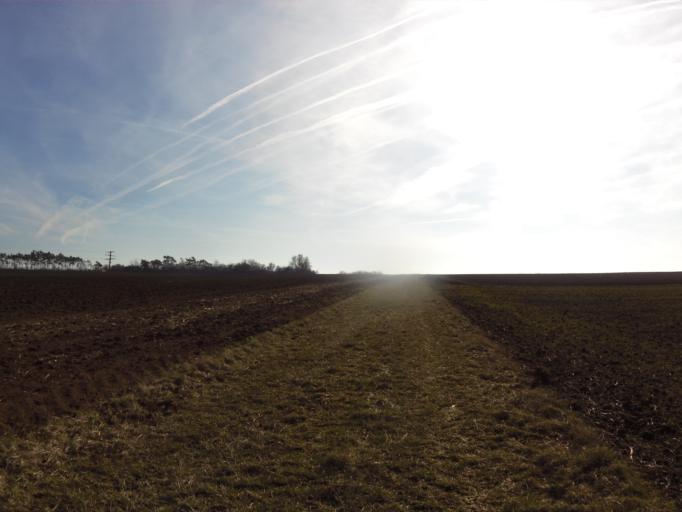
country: DE
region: Bavaria
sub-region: Regierungsbezirk Unterfranken
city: Estenfeld
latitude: 49.8272
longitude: 10.0282
